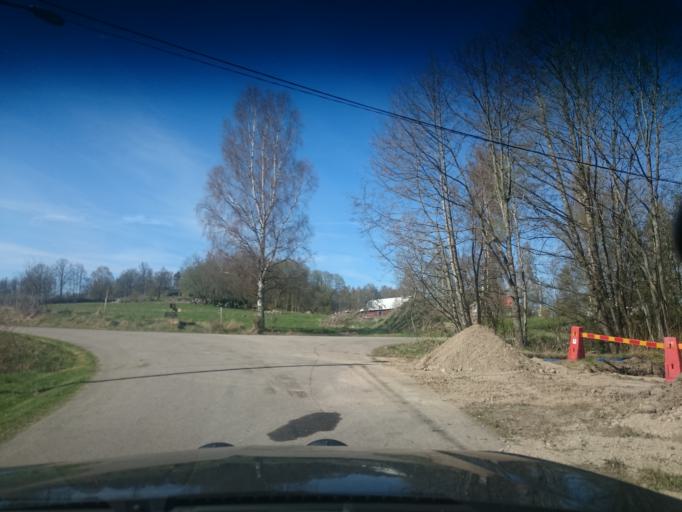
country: SE
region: Kalmar
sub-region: Hultsfreds Kommun
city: Virserum
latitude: 57.3680
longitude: 15.3941
